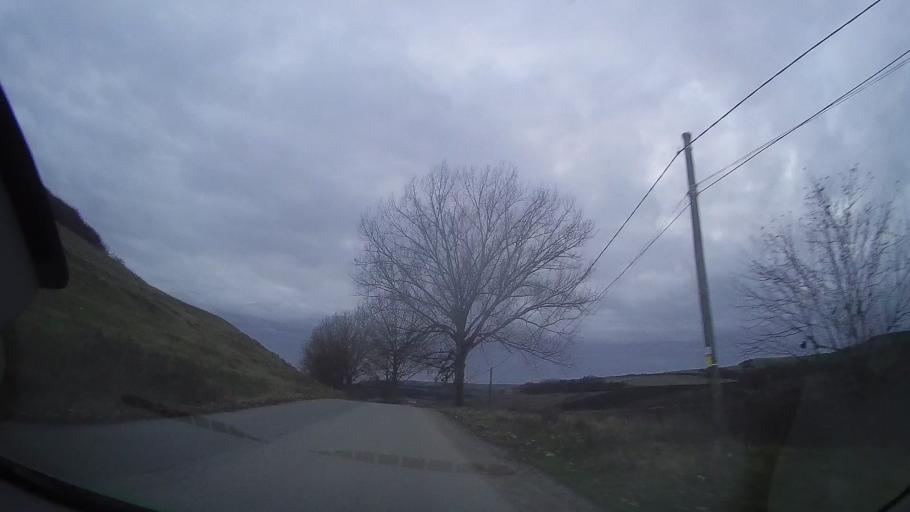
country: RO
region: Cluj
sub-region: Comuna Caianu
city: Vaida-Camaras
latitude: 46.8206
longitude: 23.9372
